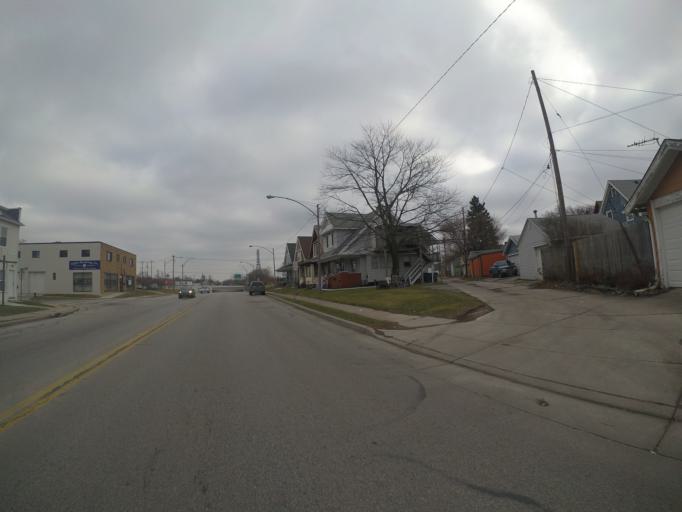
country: US
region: Ohio
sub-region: Lucas County
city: Oregon
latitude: 41.6437
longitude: -83.5010
